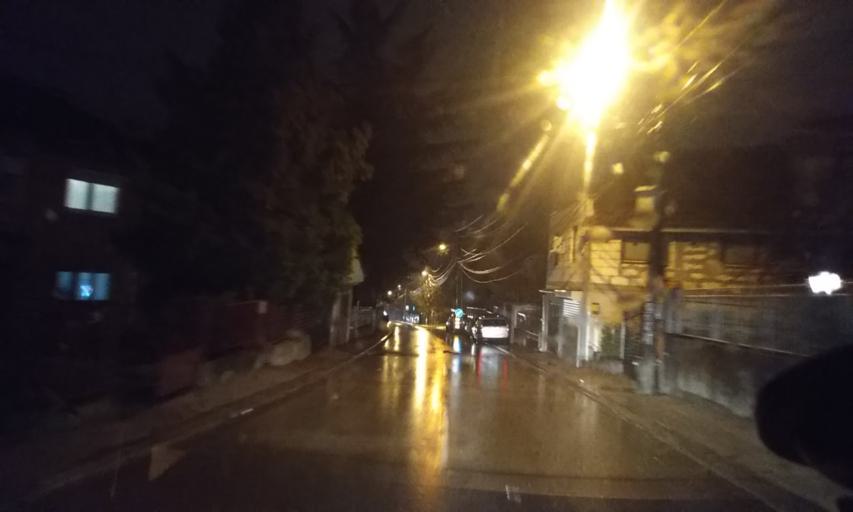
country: RS
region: Central Serbia
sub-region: Nisavski Okrug
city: Nis
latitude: 43.3078
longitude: 21.8859
